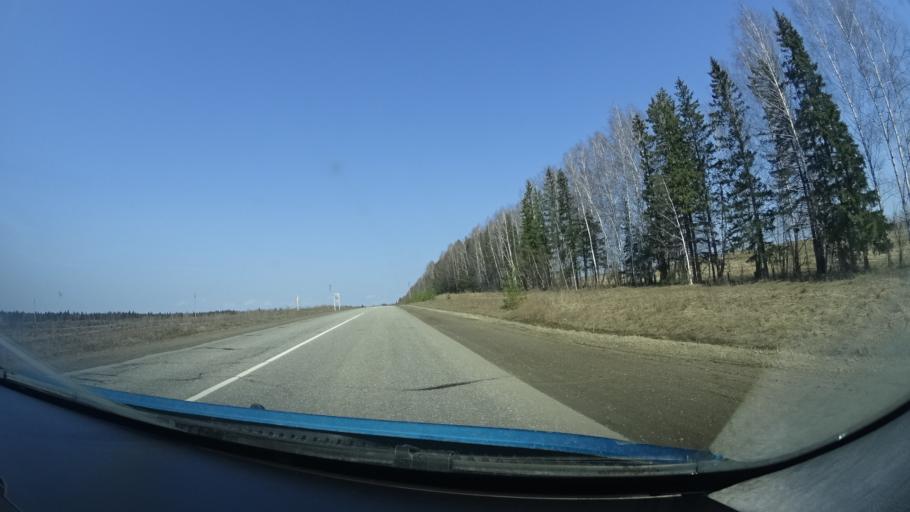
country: RU
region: Perm
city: Osa
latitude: 57.3766
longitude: 55.6096
